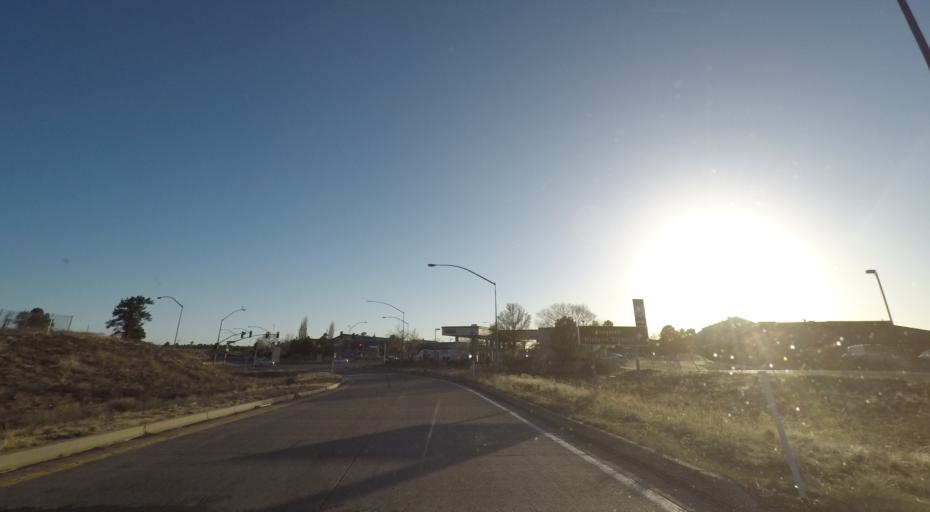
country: US
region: Arizona
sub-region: Coconino County
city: Flagstaff
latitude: 35.1927
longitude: -111.6222
